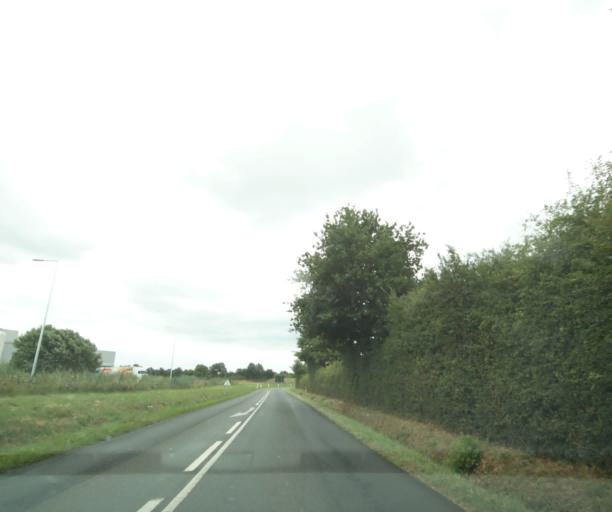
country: FR
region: Pays de la Loire
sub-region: Departement de la Sarthe
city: Sable-sur-Sarthe
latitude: 47.8250
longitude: -0.3187
